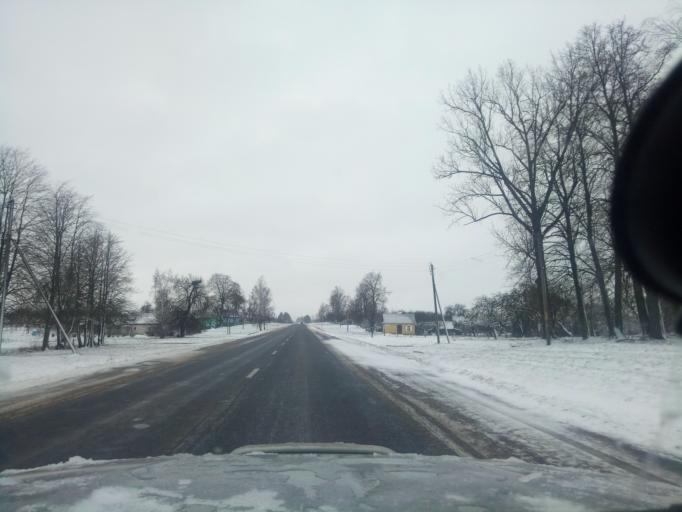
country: BY
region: Minsk
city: Klyetsk
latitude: 53.1186
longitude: 26.6642
